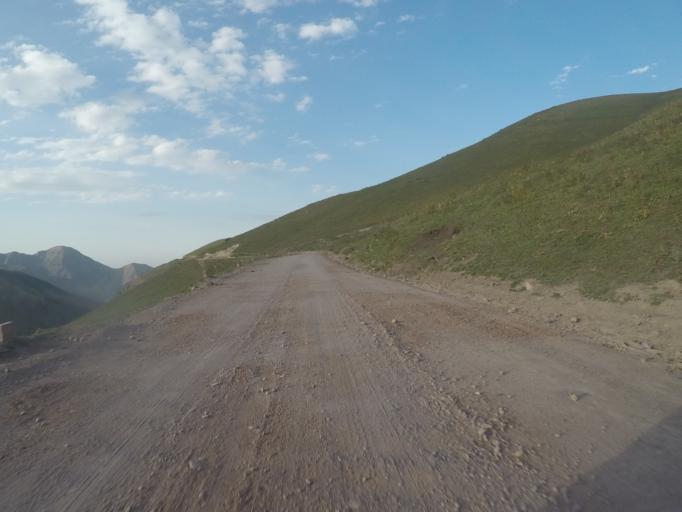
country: KG
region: Chuy
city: Bishkek
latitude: 42.6410
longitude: 74.6421
